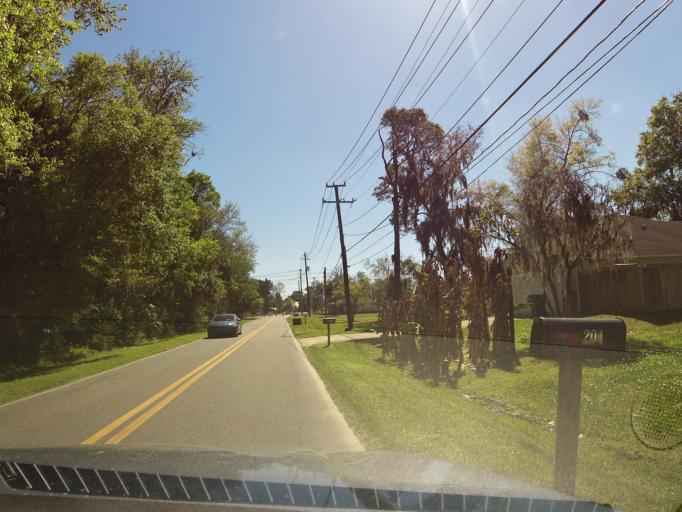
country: US
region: Florida
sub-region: Bradford County
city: Starke
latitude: 29.9443
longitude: -82.1051
